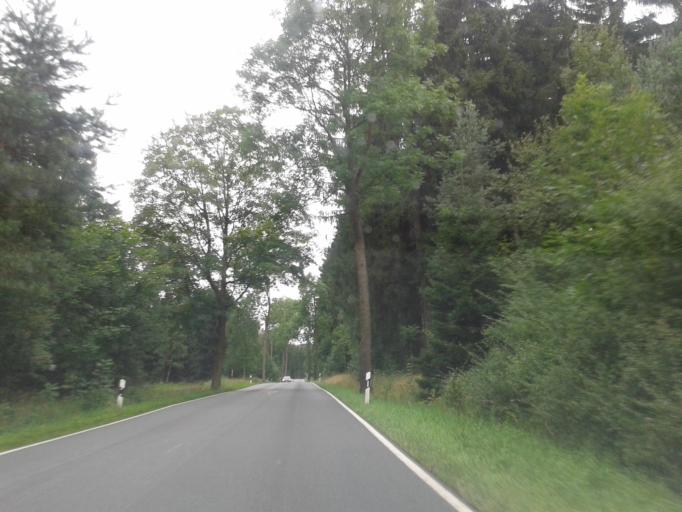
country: DE
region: Saxony
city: Tharandt
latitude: 50.9718
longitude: 13.5347
